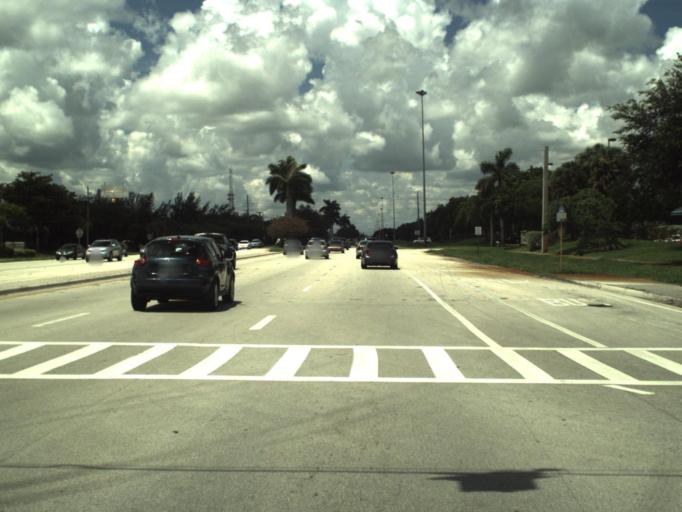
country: US
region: Florida
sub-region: Broward County
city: Miramar
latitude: 26.0088
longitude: -80.2639
